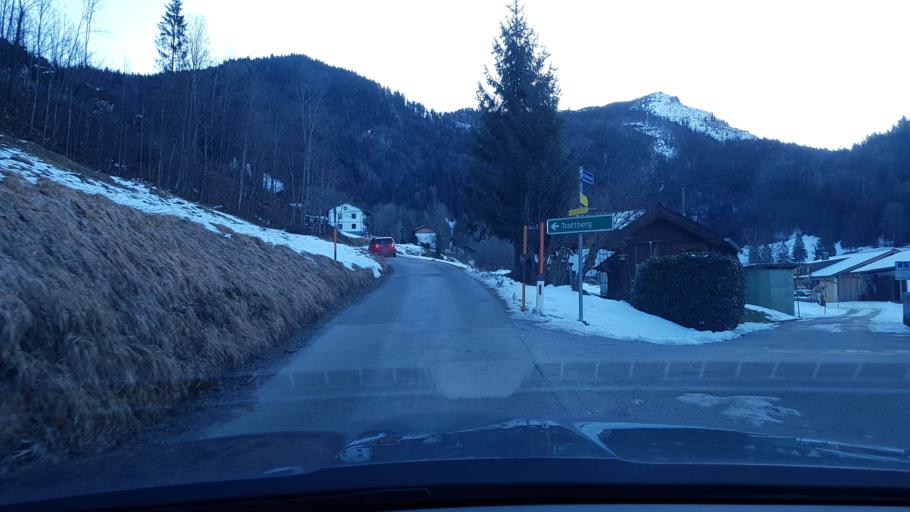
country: AT
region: Salzburg
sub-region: Politischer Bezirk Hallein
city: Scheffau am Tennengebirge
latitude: 47.6460
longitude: 13.2271
